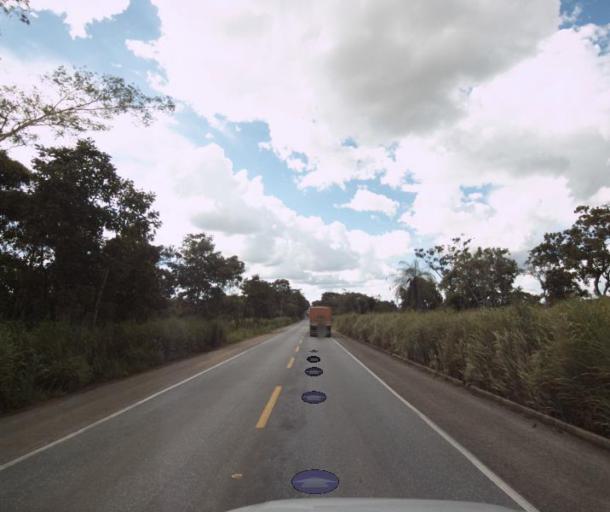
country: BR
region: Goias
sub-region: Porangatu
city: Porangatu
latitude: -13.2641
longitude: -49.1339
